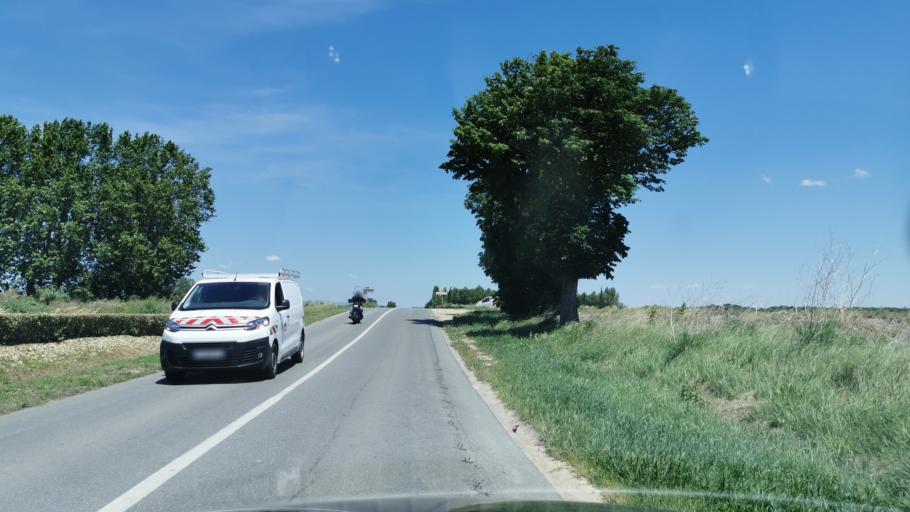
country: FR
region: Languedoc-Roussillon
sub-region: Departement de l'Aude
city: Ouveillan
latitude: 43.2514
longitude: 3.0034
